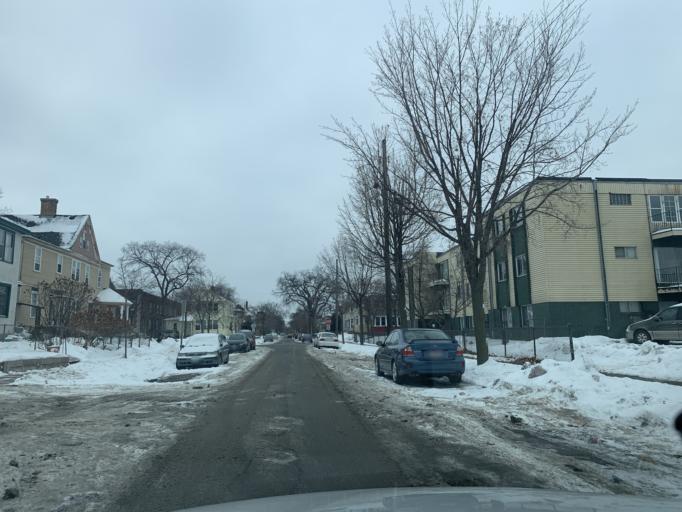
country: US
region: Minnesota
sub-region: Hennepin County
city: Minneapolis
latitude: 44.9538
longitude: -93.2787
